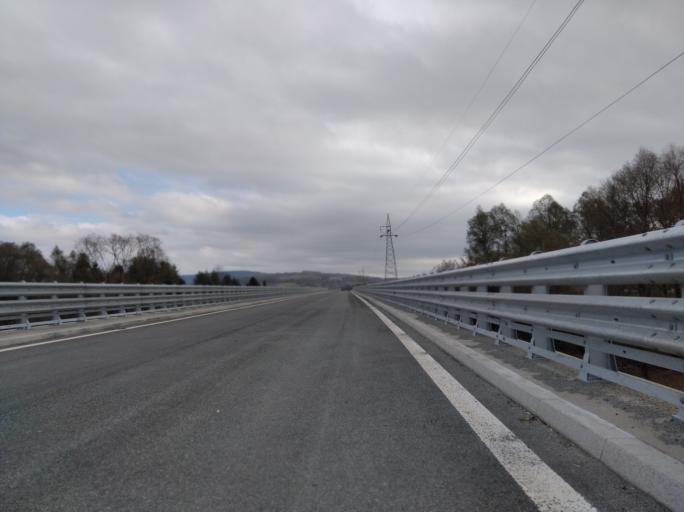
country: PL
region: Subcarpathian Voivodeship
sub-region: Powiat strzyzowski
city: Strzyzow
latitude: 49.8645
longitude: 21.7774
